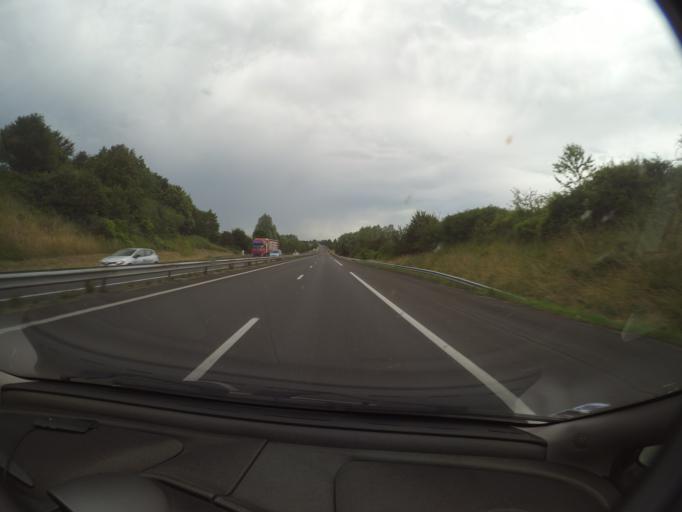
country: FR
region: Pays de la Loire
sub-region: Departement de la Sarthe
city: Noyen-sur-Sarthe
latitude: 47.9005
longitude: -0.0984
